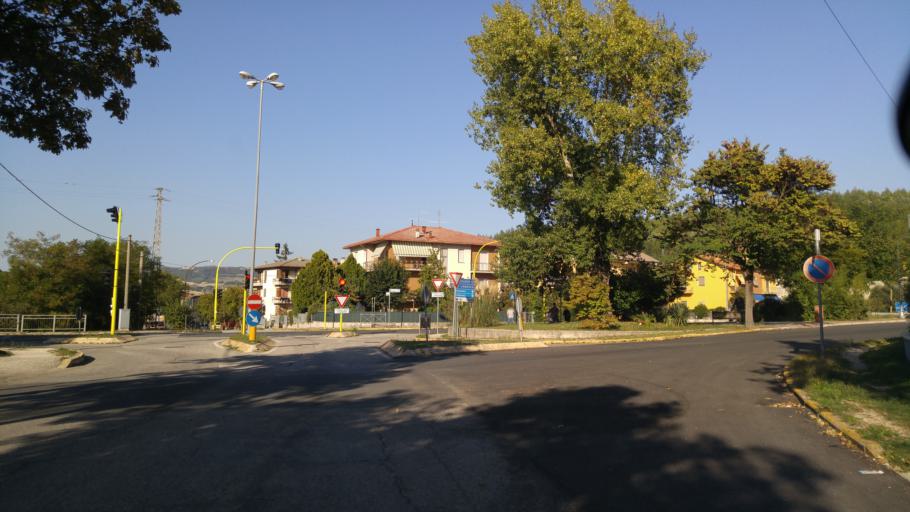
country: IT
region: The Marches
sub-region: Provincia di Pesaro e Urbino
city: Fermignano
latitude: 43.6729
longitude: 12.6449
